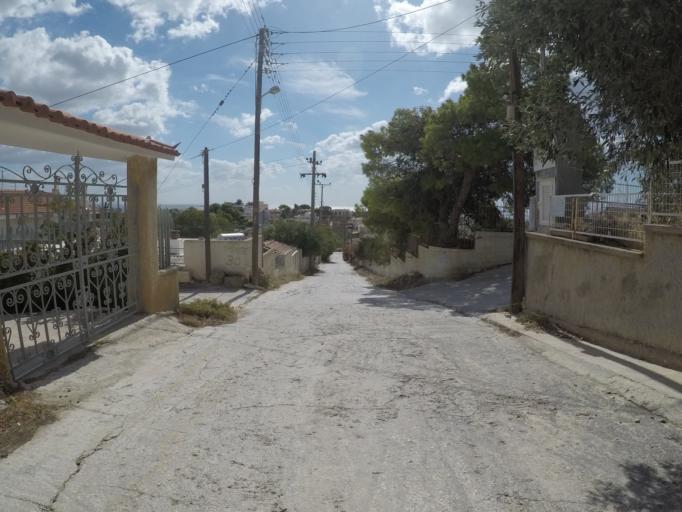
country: GR
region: Attica
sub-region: Nomarchia Anatolikis Attikis
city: Agios Dimitrios Kropias
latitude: 37.7974
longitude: 23.8772
